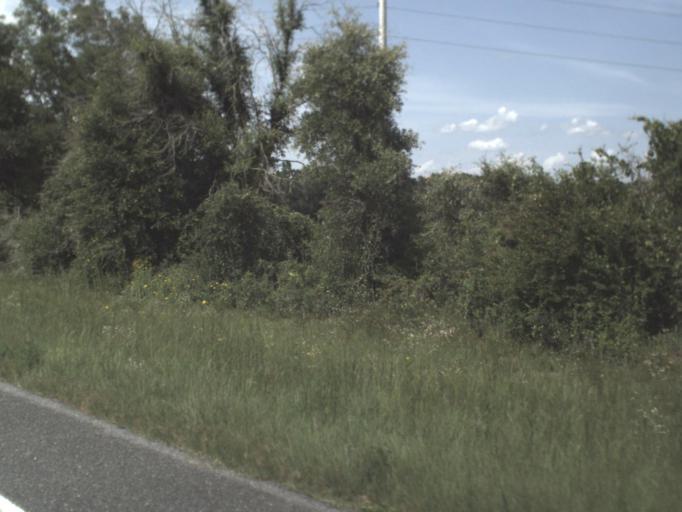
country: US
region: Florida
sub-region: Gilchrist County
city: Trenton
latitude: 29.7511
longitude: -82.7406
